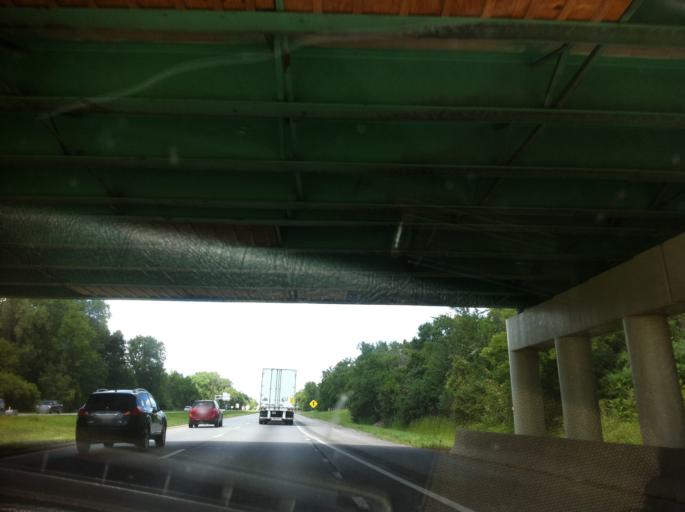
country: US
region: Ohio
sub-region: Lucas County
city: Sylvania
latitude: 41.7152
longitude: -83.6881
